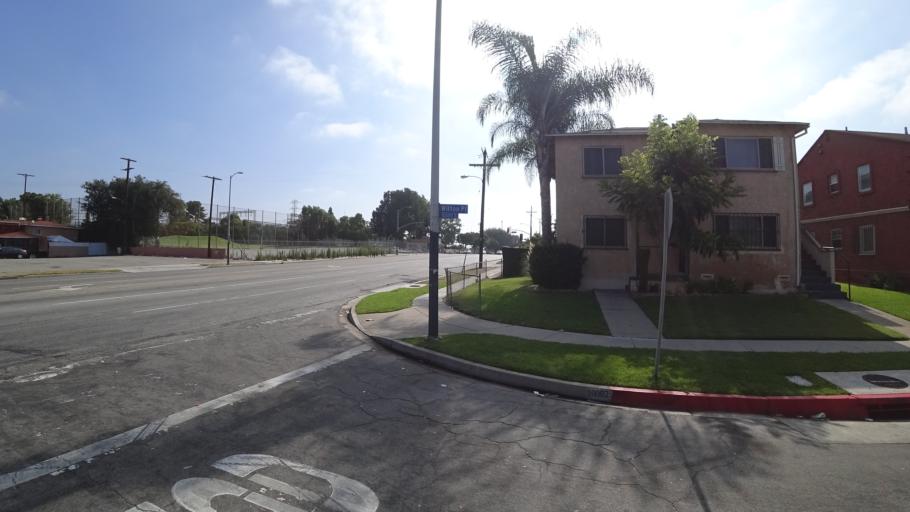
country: US
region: California
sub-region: Los Angeles County
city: Westmont
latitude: 33.9453
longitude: -118.3144
